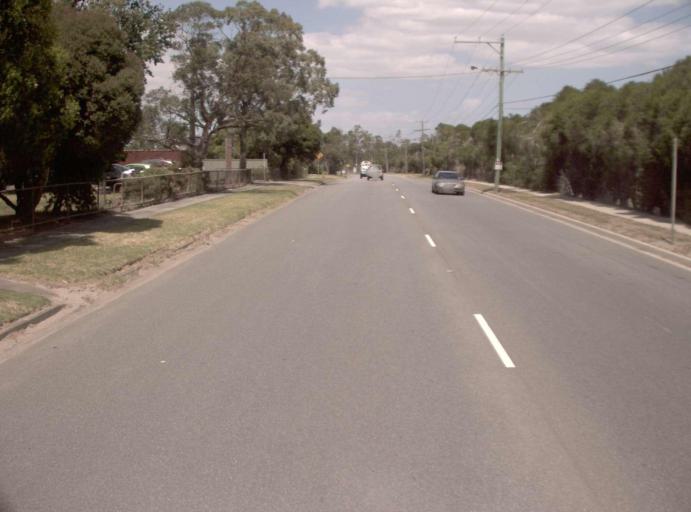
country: AU
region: Victoria
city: Heatherton
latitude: -37.9587
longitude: 145.1012
